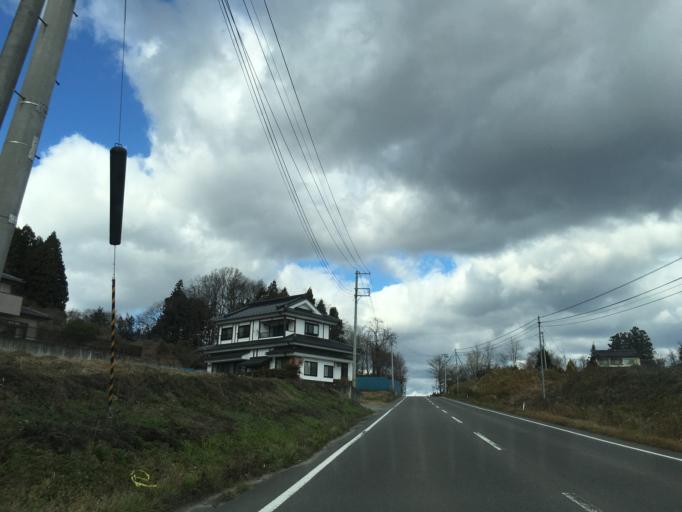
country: JP
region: Fukushima
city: Sukagawa
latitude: 37.3253
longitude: 140.4403
